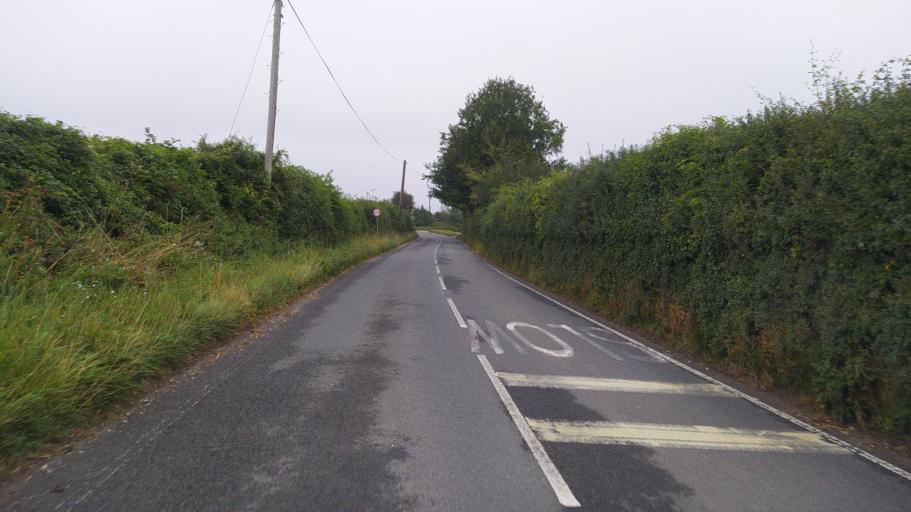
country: GB
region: England
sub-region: Wiltshire
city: Bower Chalke
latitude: 50.9562
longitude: -2.0151
